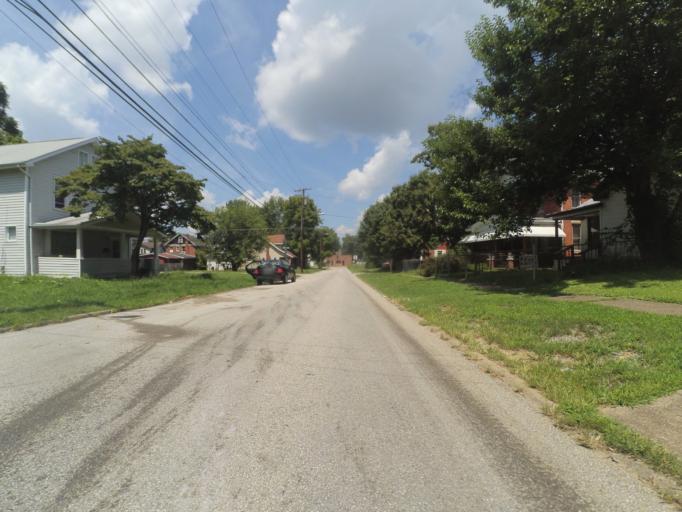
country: US
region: West Virginia
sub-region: Cabell County
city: Huntington
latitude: 38.4115
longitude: -82.4233
